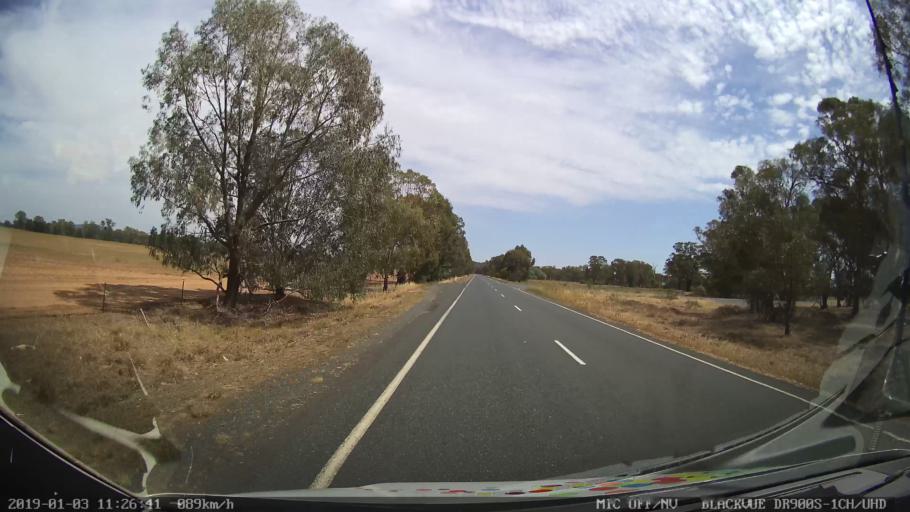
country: AU
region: New South Wales
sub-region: Weddin
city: Grenfell
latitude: -34.0219
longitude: 148.2236
